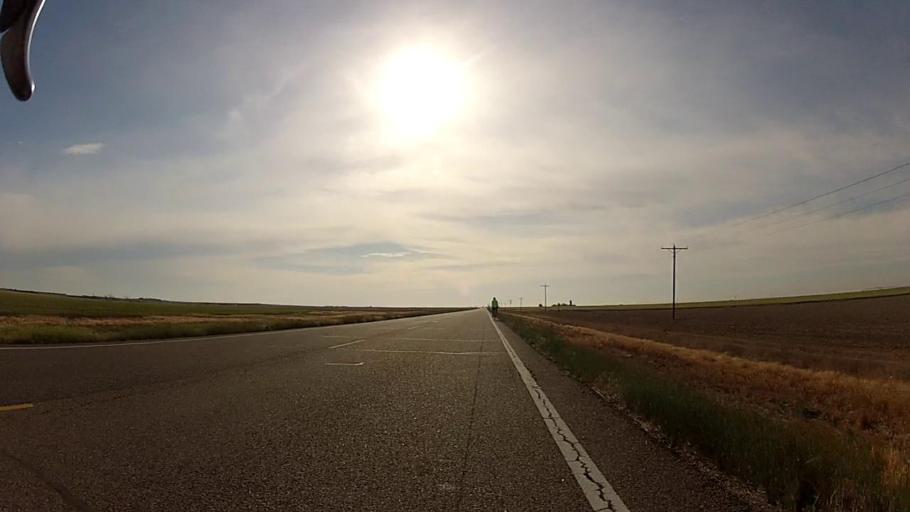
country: US
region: Kansas
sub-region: Grant County
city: Ulysses
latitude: 37.5766
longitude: -101.4620
